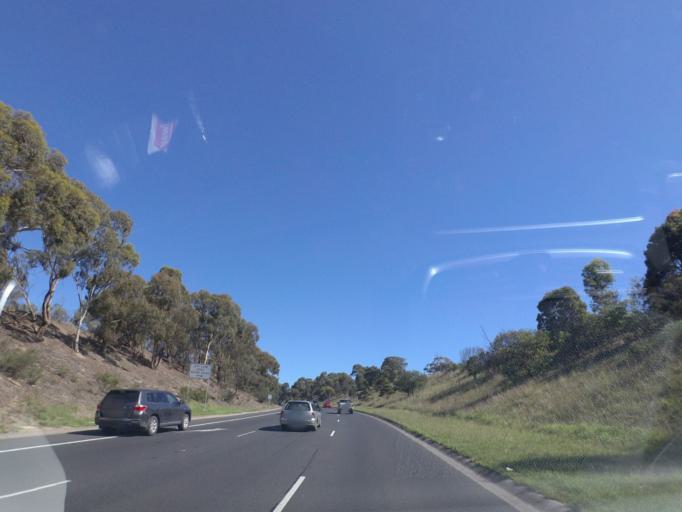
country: AU
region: Victoria
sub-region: Banyule
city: Watsonia North
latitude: -37.6947
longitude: 145.0918
